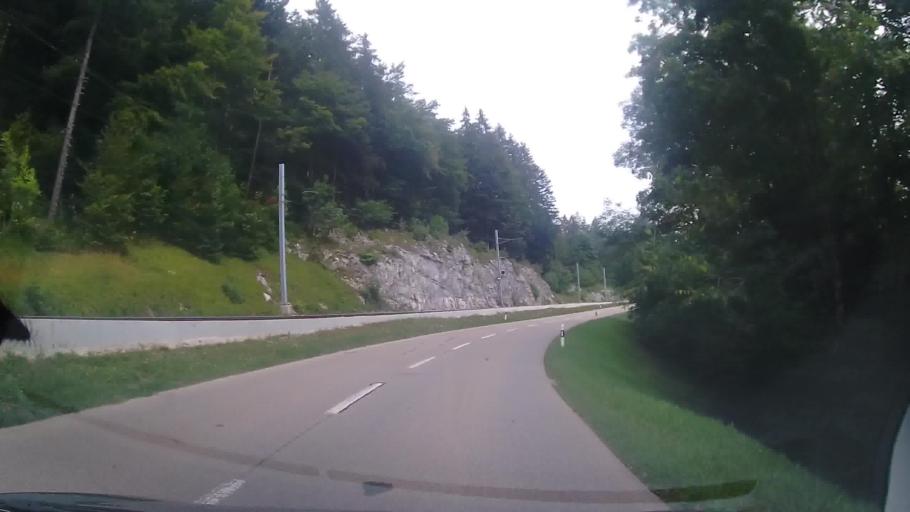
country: CH
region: Vaud
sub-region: Nyon District
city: Saint-Cergue
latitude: 46.4497
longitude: 6.1322
